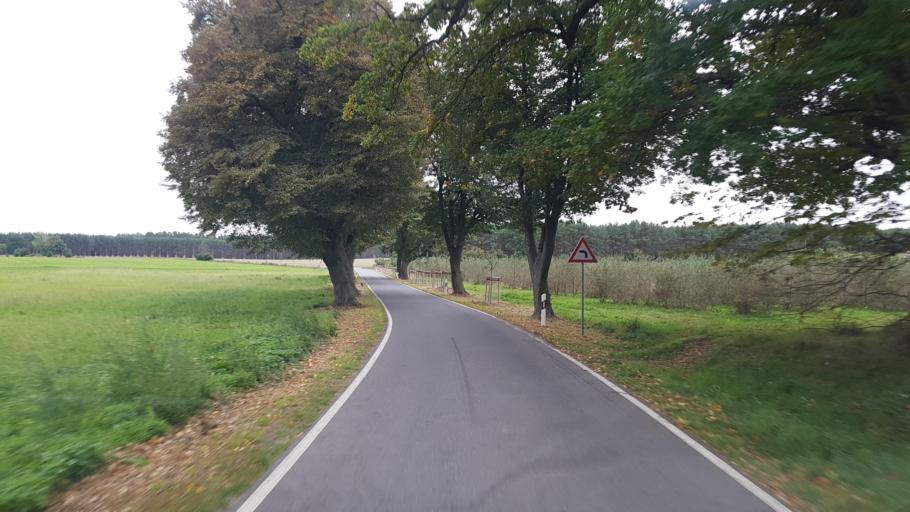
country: DE
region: Brandenburg
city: Drahnsdorf
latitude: 51.9572
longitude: 13.5420
